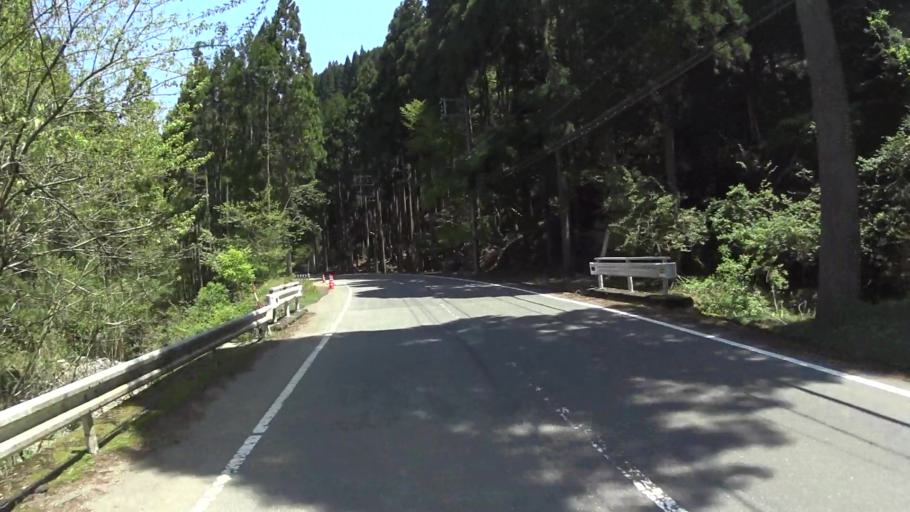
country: JP
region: Shiga Prefecture
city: Kitahama
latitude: 35.1978
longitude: 135.7847
